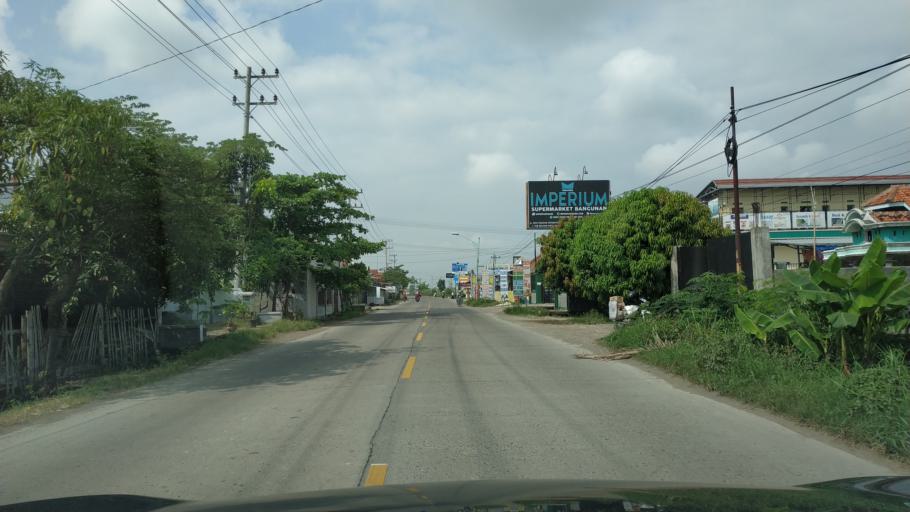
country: ID
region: Central Java
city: Ketanggungan
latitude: -6.9086
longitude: 108.8892
